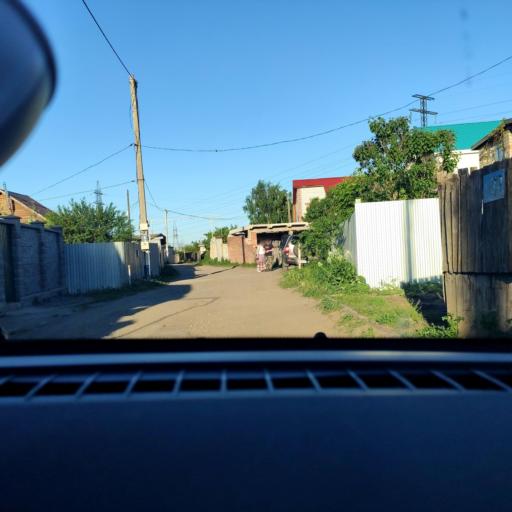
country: RU
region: Samara
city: Samara
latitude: 53.1302
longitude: 50.1845
